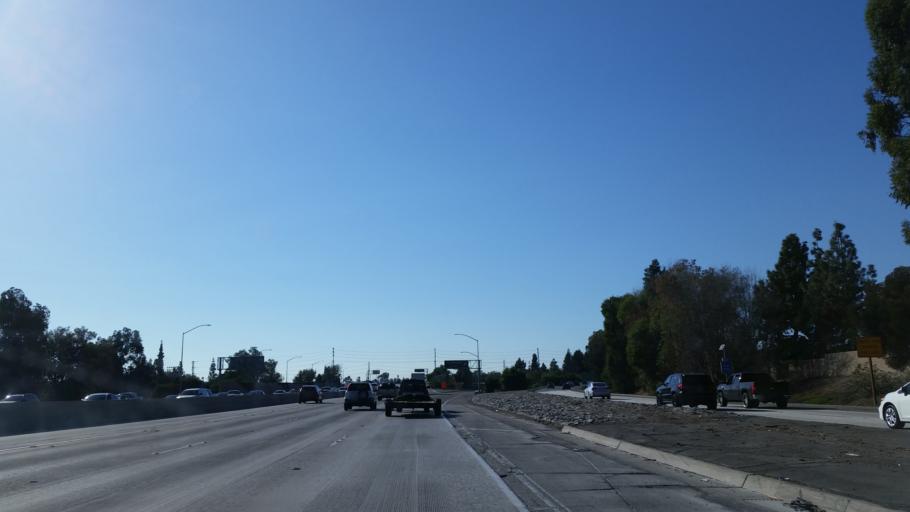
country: US
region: California
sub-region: Los Angeles County
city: Artesia
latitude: 33.8765
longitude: -118.0949
